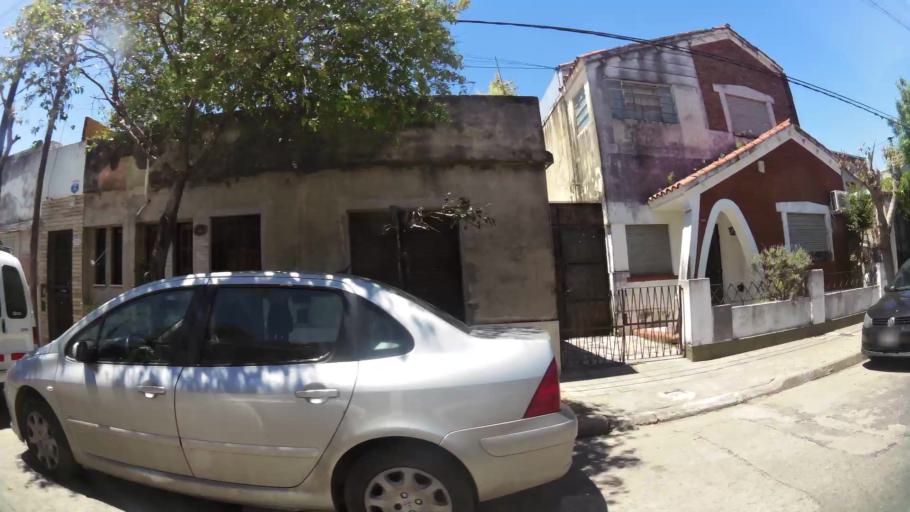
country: AR
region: Santa Fe
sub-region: Departamento de Rosario
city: Rosario
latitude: -32.9435
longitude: -60.6957
